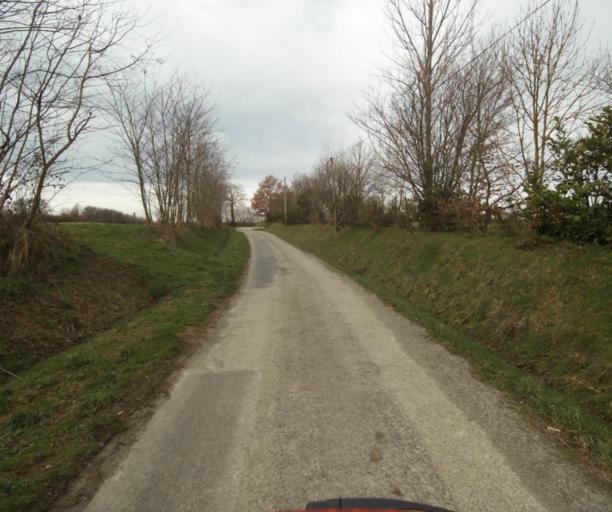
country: FR
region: Midi-Pyrenees
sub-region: Departement de l'Ariege
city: Verniolle
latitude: 43.0830
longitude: 1.7048
